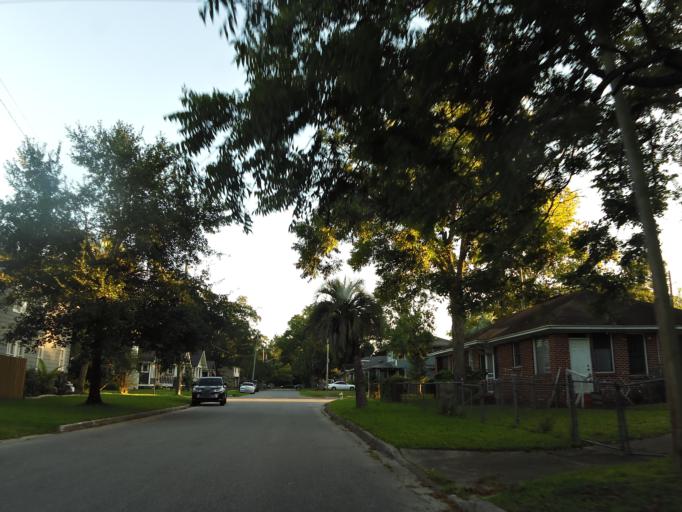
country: US
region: Florida
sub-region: Duval County
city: Jacksonville
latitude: 30.3156
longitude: -81.6990
